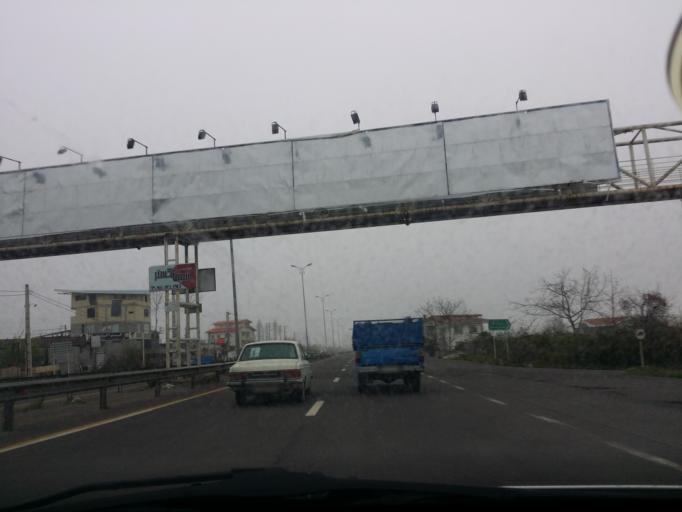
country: IR
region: Mazandaran
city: Tonekabon
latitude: 36.8231
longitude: 50.8462
